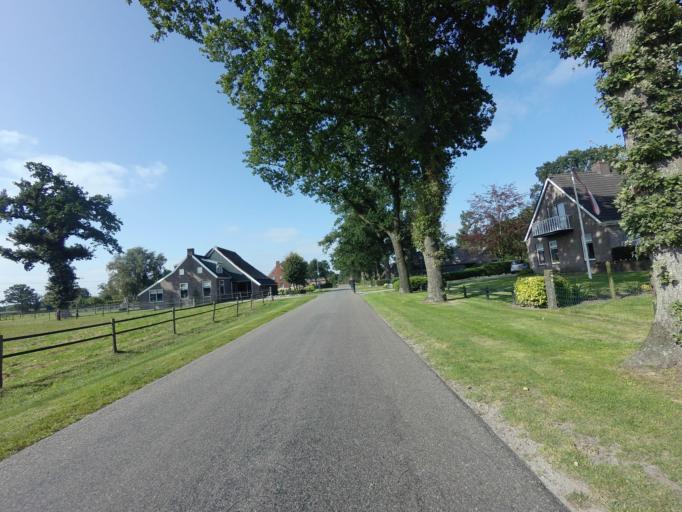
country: NL
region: Drenthe
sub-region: Gemeente Tynaarlo
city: Vries
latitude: 53.0580
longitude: 6.4978
